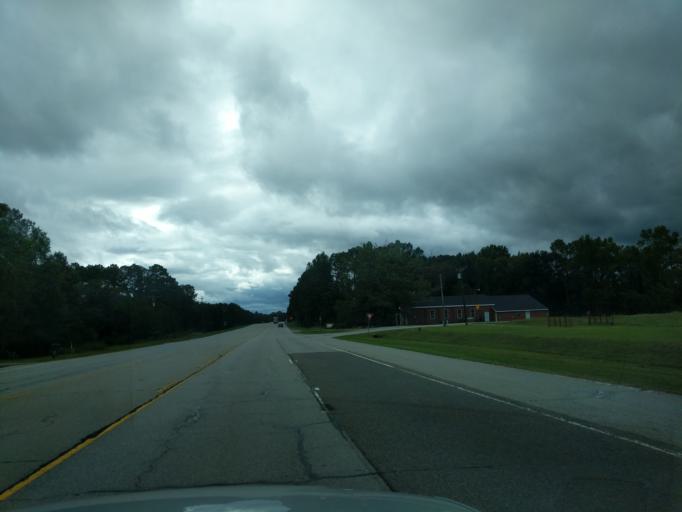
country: US
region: Georgia
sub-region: Wilkes County
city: Washington
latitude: 33.7067
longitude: -82.6959
